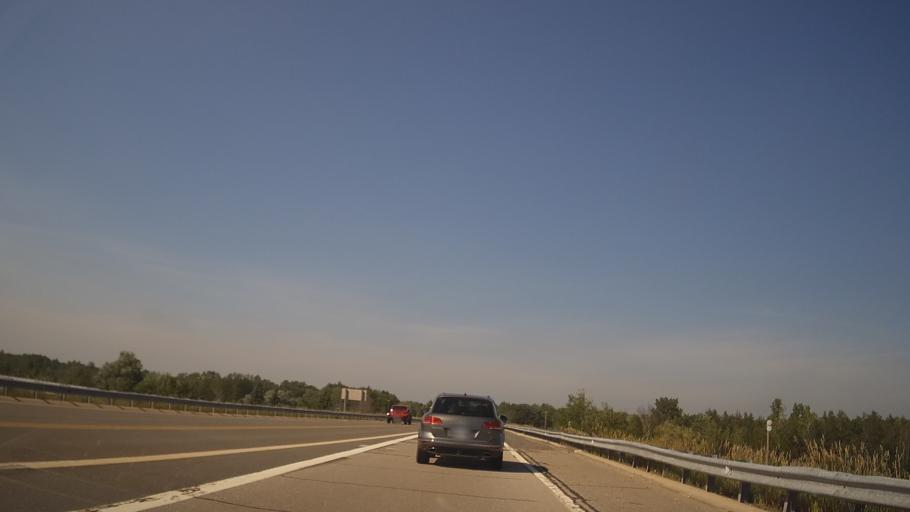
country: US
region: Michigan
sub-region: Ogemaw County
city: Skidway Lake
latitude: 44.1337
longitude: -84.1297
